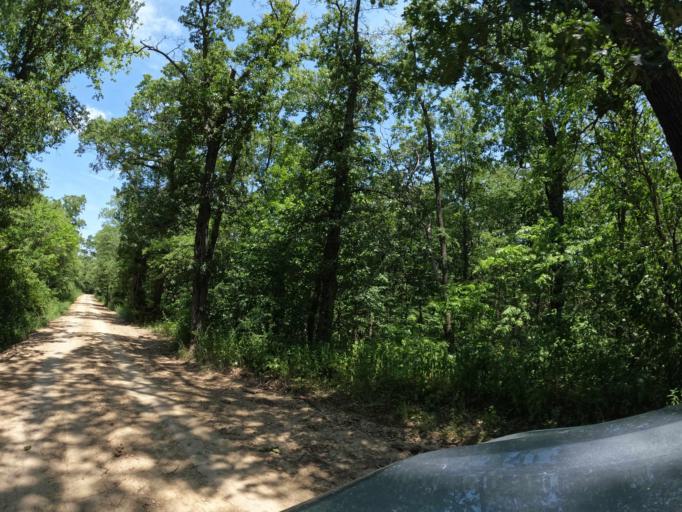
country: US
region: Iowa
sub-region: Henry County
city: Mount Pleasant
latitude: 40.9204
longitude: -91.6652
